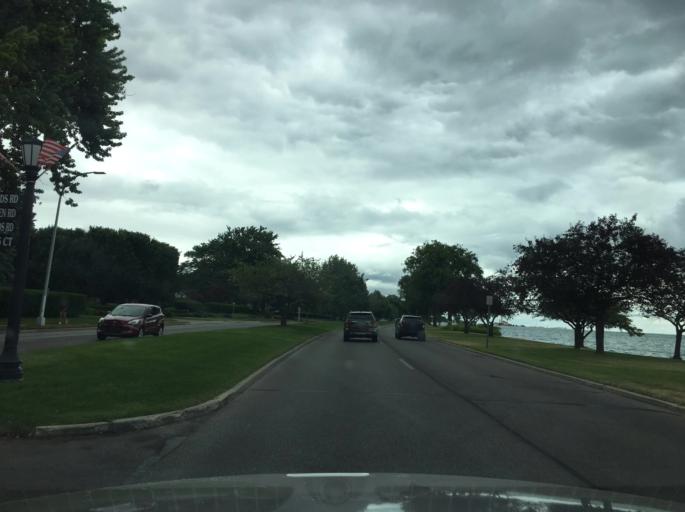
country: US
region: Michigan
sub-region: Wayne County
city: Grosse Pointe Farms
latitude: 42.4194
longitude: -82.8819
